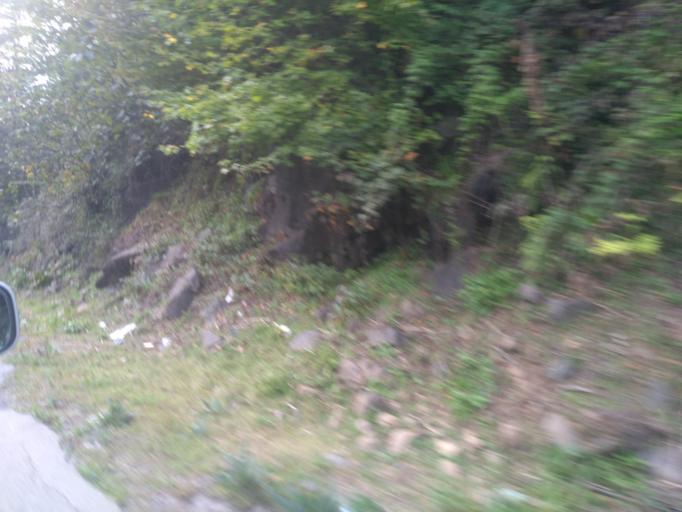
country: GE
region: Ajaria
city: Keda
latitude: 41.5683
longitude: 41.8437
